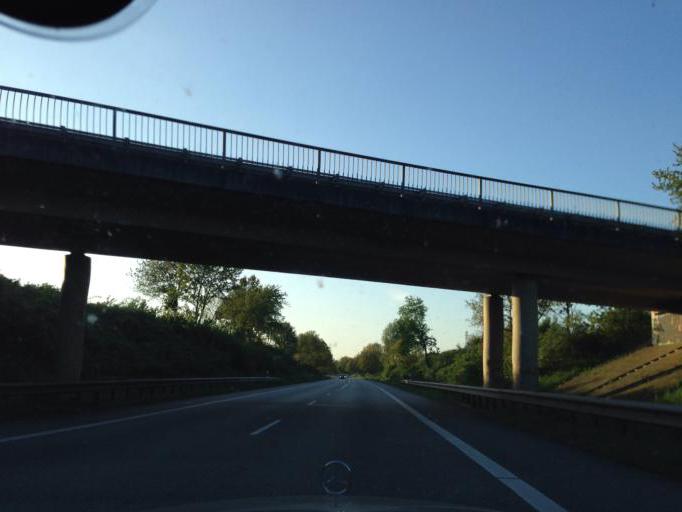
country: DE
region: Schleswig-Holstein
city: Rickling
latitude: 54.0017
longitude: 10.1807
